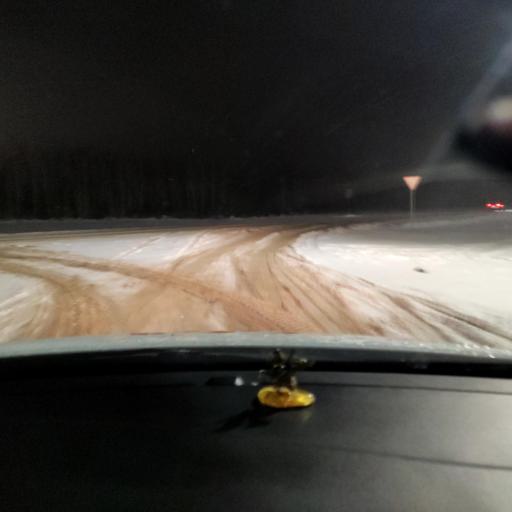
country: RU
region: Tatarstan
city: Stolbishchi
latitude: 55.6226
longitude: 49.2297
